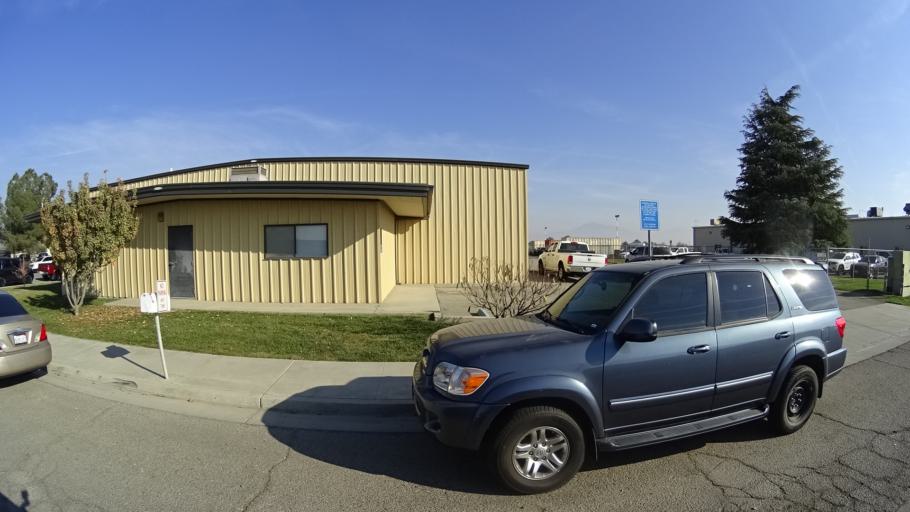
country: US
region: California
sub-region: Kern County
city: Bakersfield
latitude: 35.3246
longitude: -118.9997
